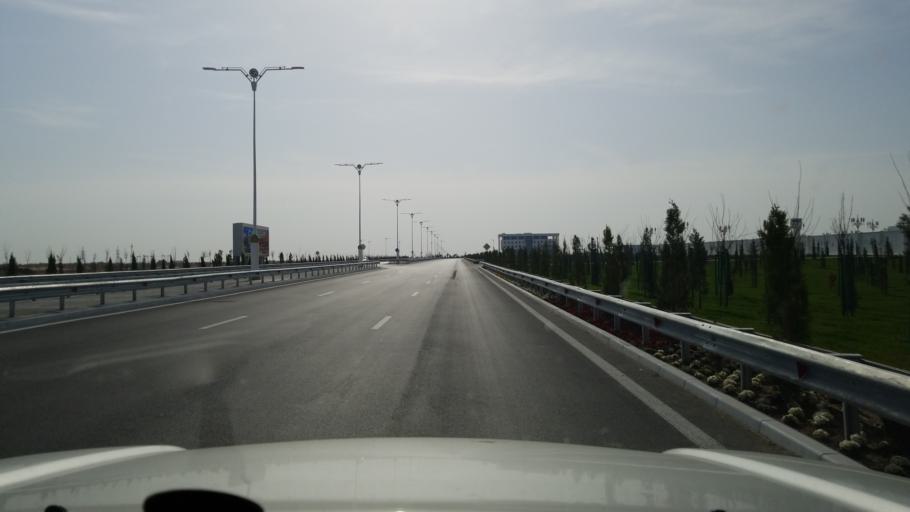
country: TM
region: Lebap
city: Turkmenabat
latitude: 38.9431
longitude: 63.5670
